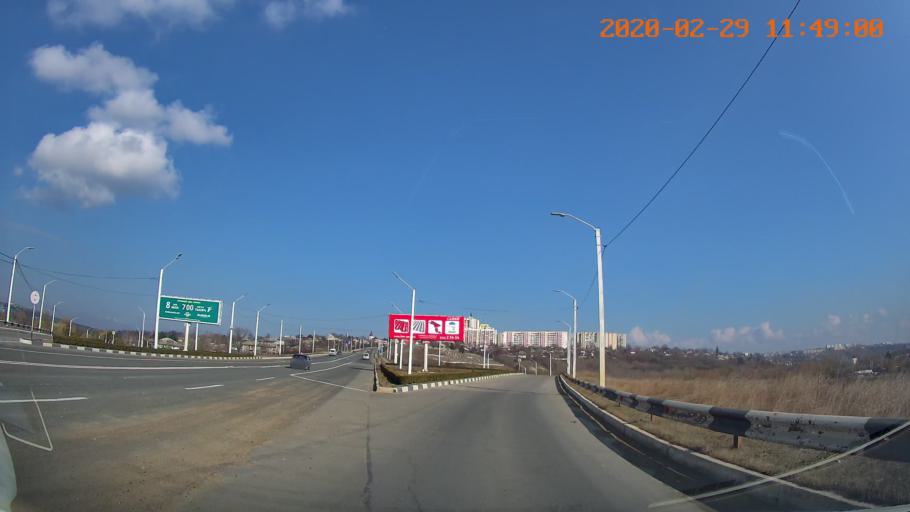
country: MD
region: Telenesti
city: Ribnita
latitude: 47.7520
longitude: 28.9942
